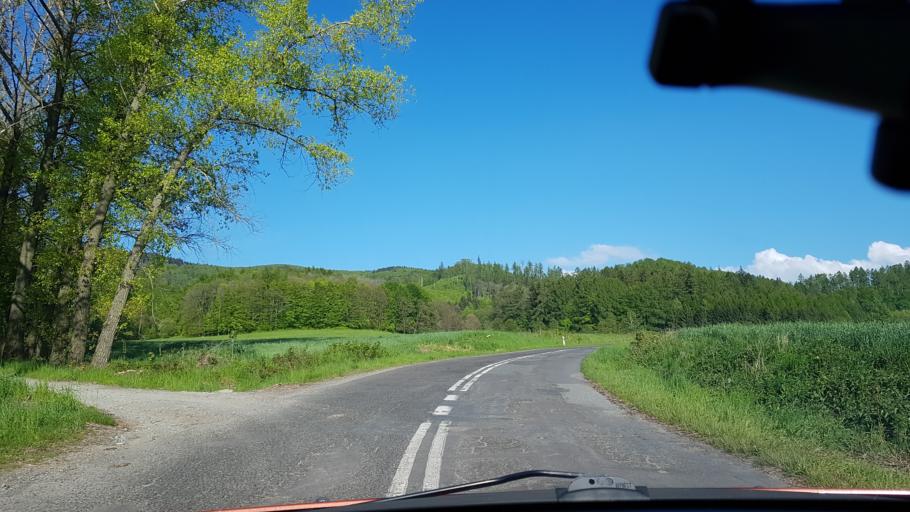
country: PL
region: Lower Silesian Voivodeship
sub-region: Powiat klodzki
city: Jugow
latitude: 50.5874
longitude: 16.5799
